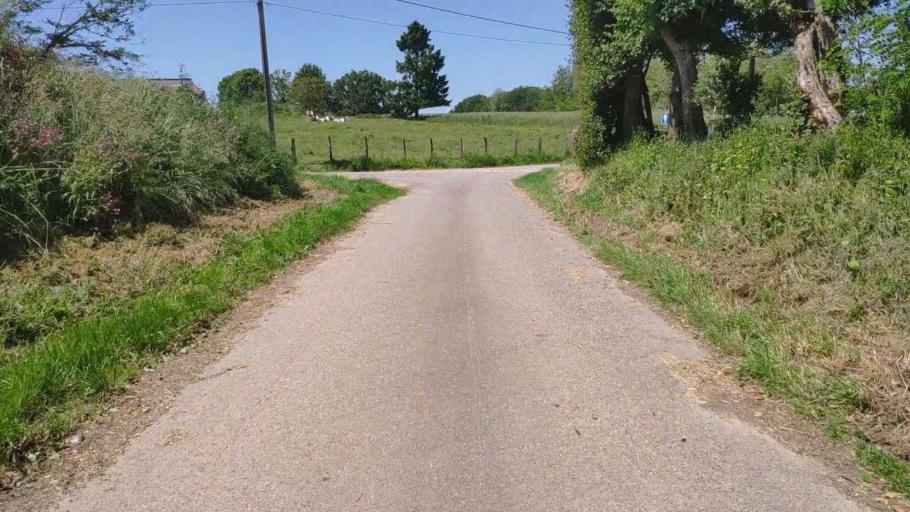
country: FR
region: Franche-Comte
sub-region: Departement du Jura
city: Bletterans
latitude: 46.7486
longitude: 5.3952
